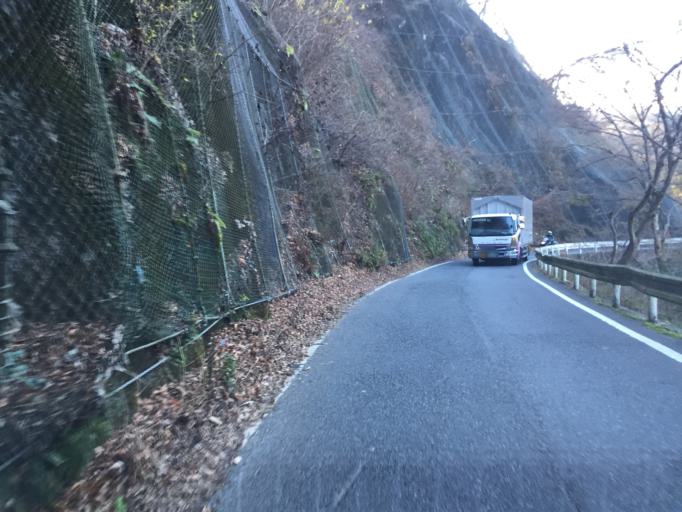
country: JP
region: Fukushima
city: Iwaki
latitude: 37.1709
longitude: 140.8289
